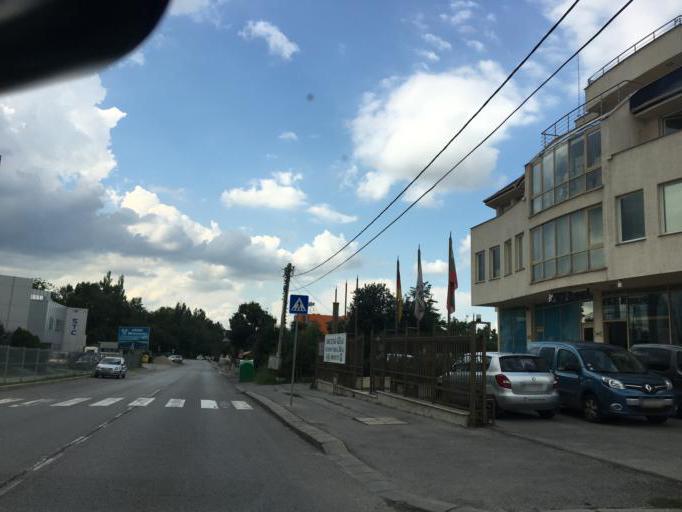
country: BG
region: Sofia-Capital
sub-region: Stolichna Obshtina
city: Sofia
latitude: 42.6294
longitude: 23.3569
